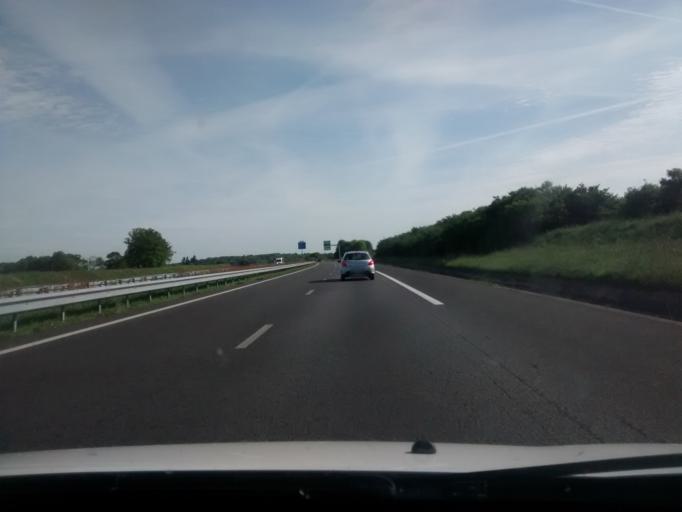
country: FR
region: Brittany
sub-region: Departement d'Ille-et-Vilaine
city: Saint-Sauveur-des-Landes
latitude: 48.3300
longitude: -1.3030
